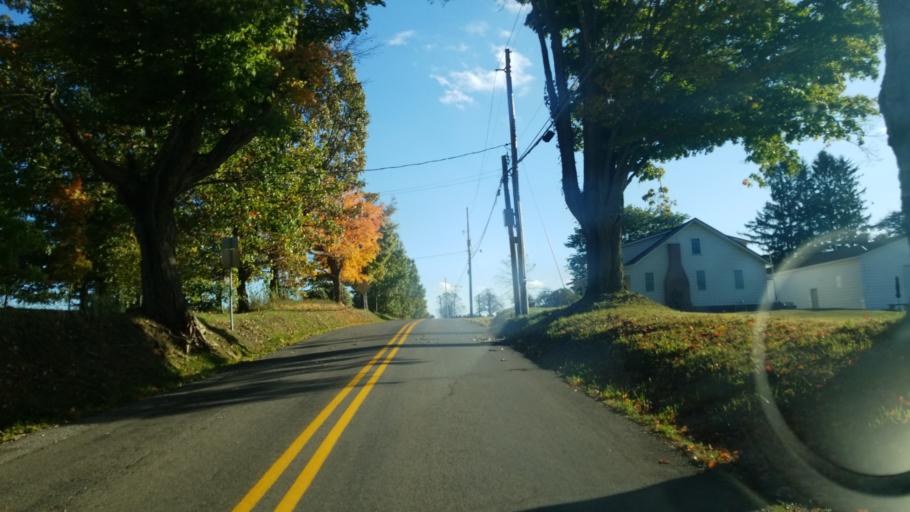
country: US
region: Pennsylvania
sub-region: Indiana County
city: Johnsonburg
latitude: 40.9237
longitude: -78.8843
